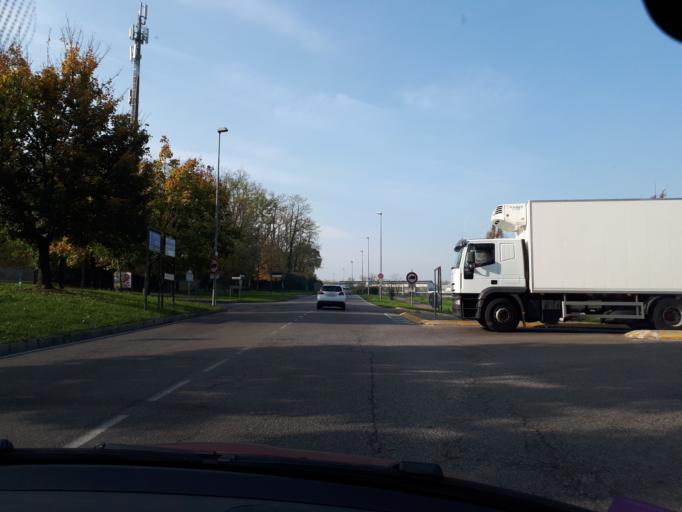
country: IT
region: Lombardy
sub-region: Provincia di Monza e Brianza
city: Lesmo
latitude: 45.6328
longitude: 9.2974
